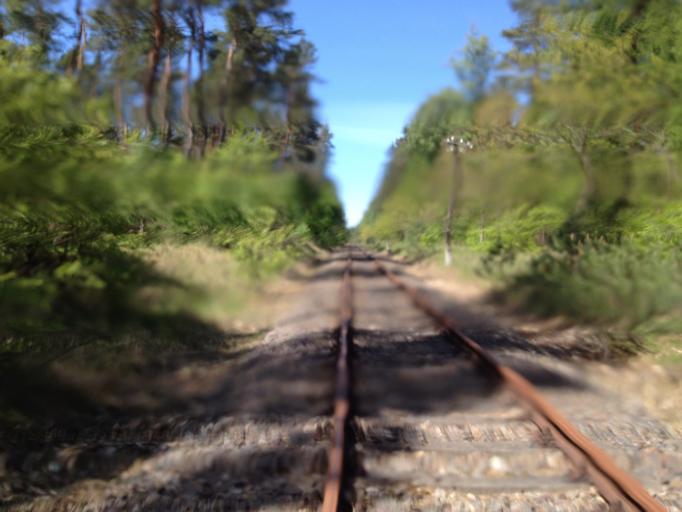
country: DE
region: Brandenburg
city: Lychen
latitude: 53.1634
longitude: 13.3771
